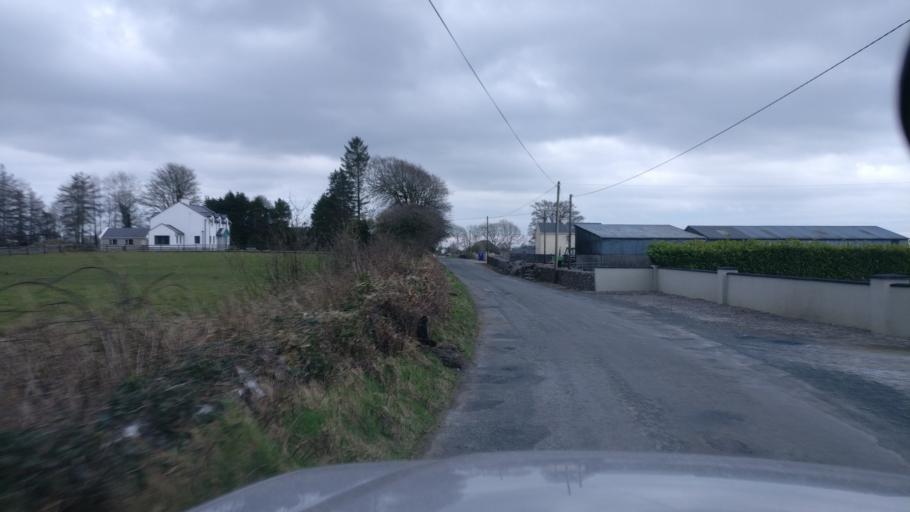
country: IE
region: Connaught
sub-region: County Galway
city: Loughrea
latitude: 53.2666
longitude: -8.4688
